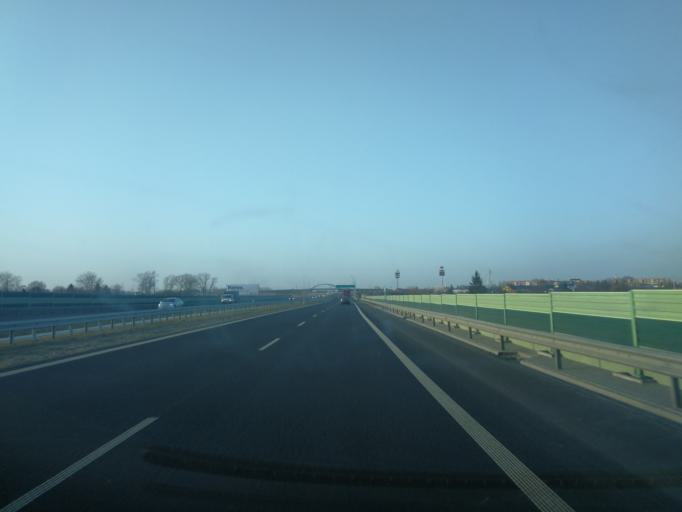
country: PL
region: Pomeranian Voivodeship
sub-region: Powiat nowodworski
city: Nowy Dwor Gdanski
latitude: 54.2052
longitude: 19.1098
